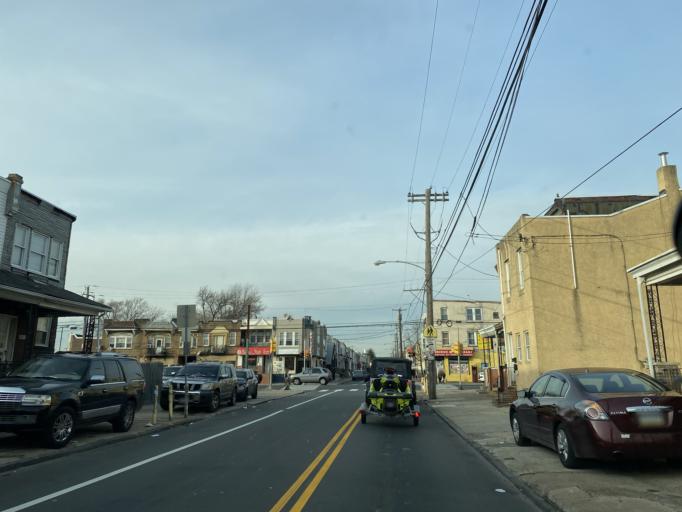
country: US
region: New Jersey
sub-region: Burlington County
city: Palmyra
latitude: 40.0127
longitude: -75.0703
